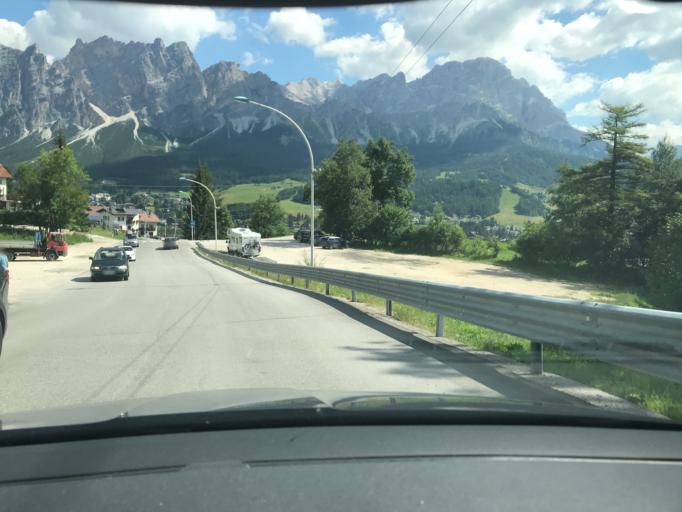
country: IT
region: Veneto
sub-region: Provincia di Belluno
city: Cortina d'Ampezzo
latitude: 46.5353
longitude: 12.1238
